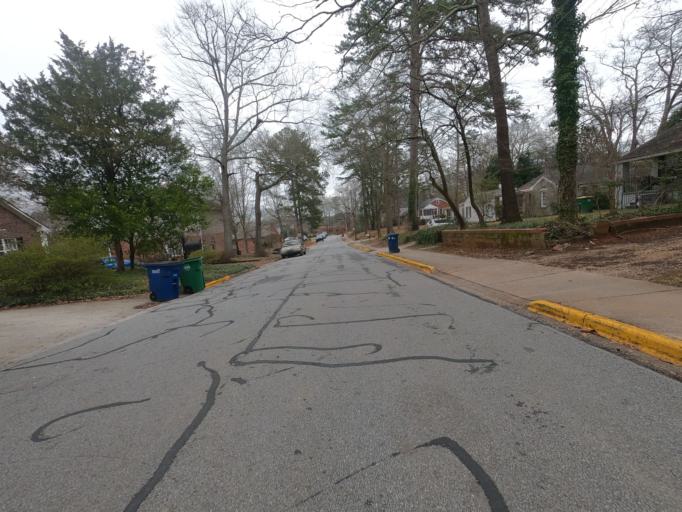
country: US
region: Georgia
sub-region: Clarke County
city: Athens
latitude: 33.9386
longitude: -83.3784
